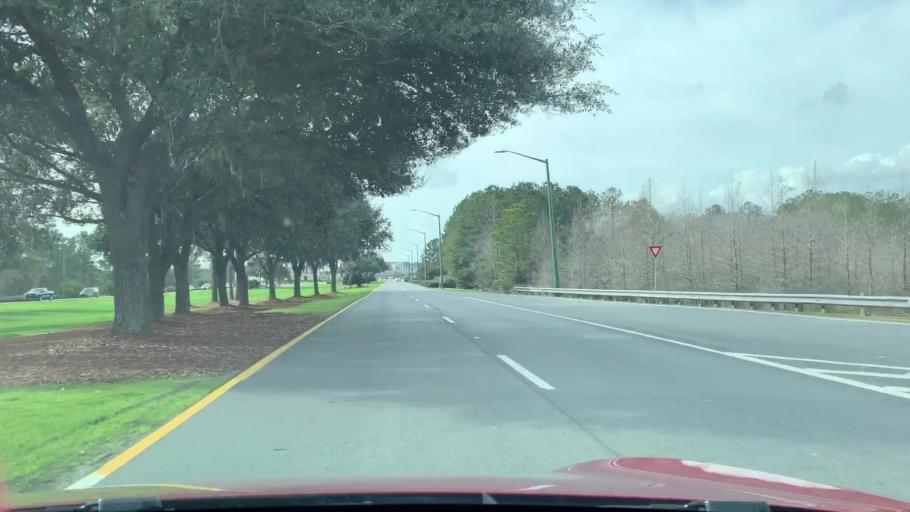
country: US
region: Georgia
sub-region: Chatham County
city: Pooler
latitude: 32.1383
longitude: -81.2270
